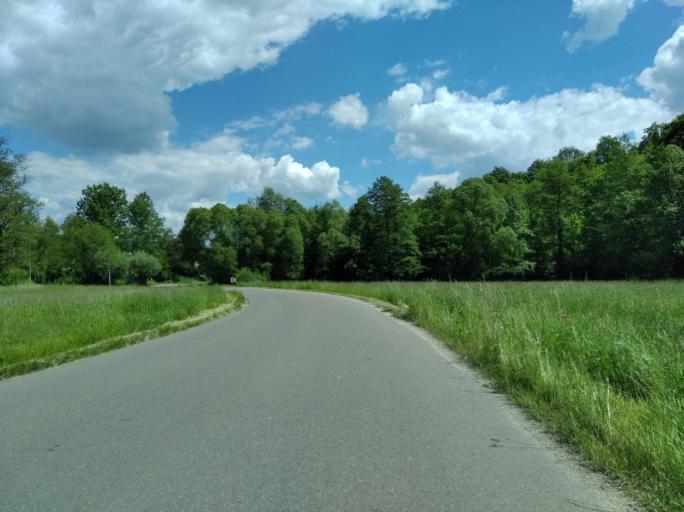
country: PL
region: Subcarpathian Voivodeship
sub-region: Powiat krosnienski
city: Leki
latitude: 49.7853
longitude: 21.6197
